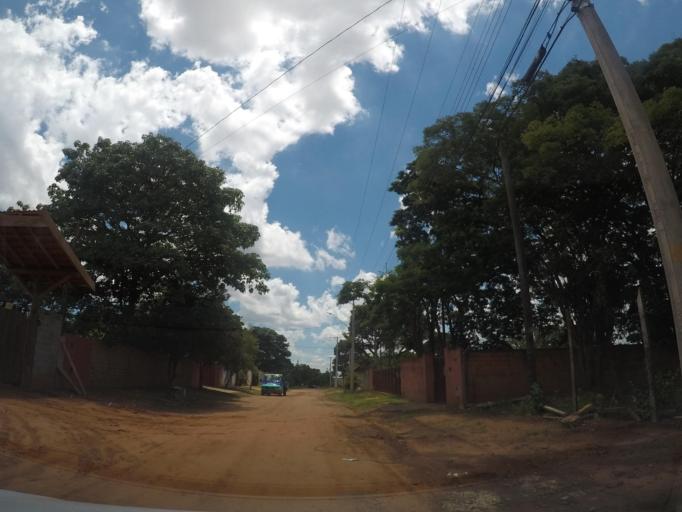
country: BR
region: Sao Paulo
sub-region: Hortolandia
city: Hortolandia
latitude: -22.8405
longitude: -47.2339
